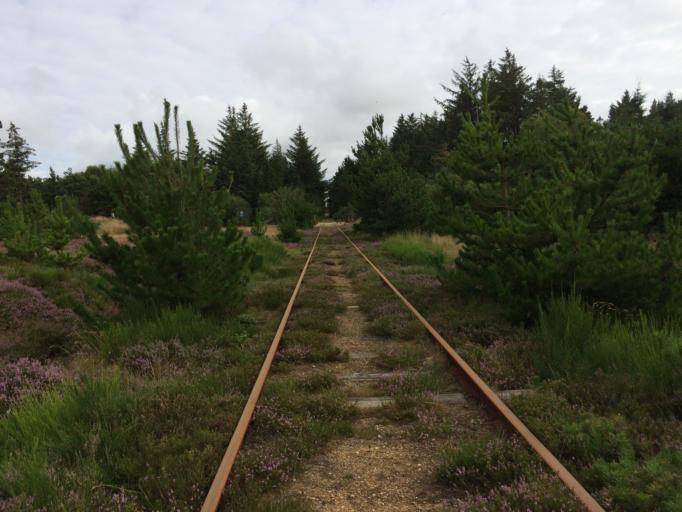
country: DK
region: South Denmark
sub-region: Varde Kommune
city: Oksbol
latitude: 55.7996
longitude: 8.2222
